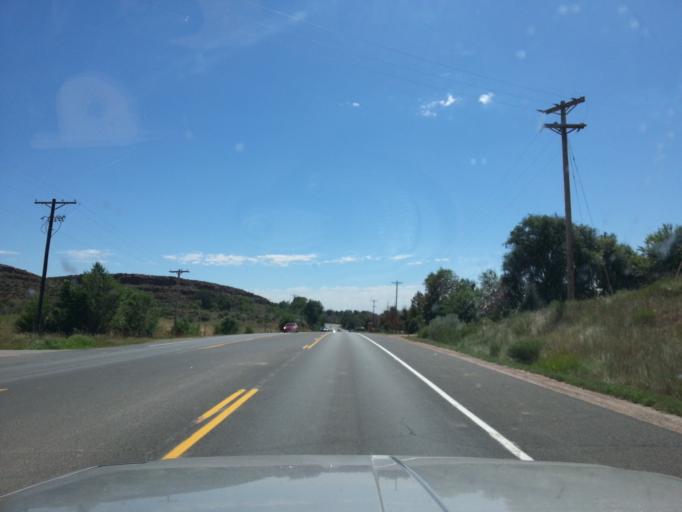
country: US
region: Colorado
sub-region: Larimer County
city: Loveland
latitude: 40.4075
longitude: -105.1496
